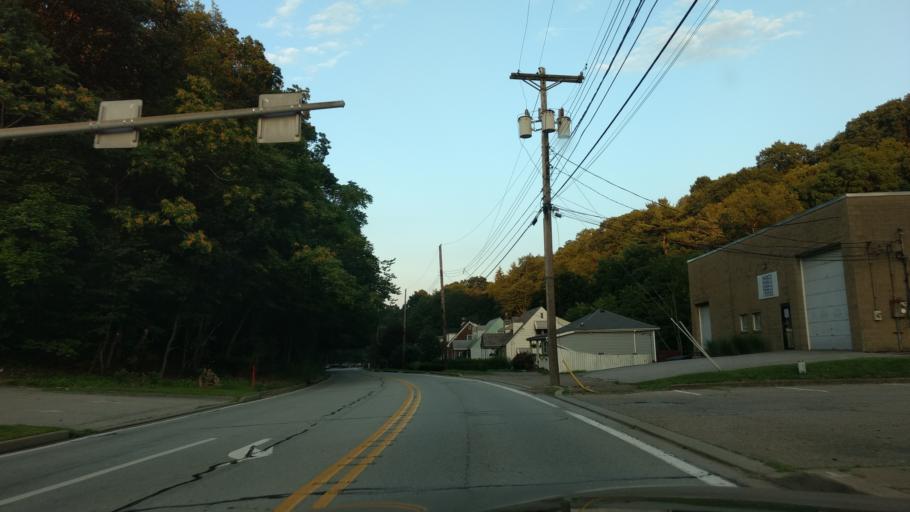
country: US
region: Pennsylvania
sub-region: Allegheny County
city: West View
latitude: 40.5207
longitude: -80.0250
